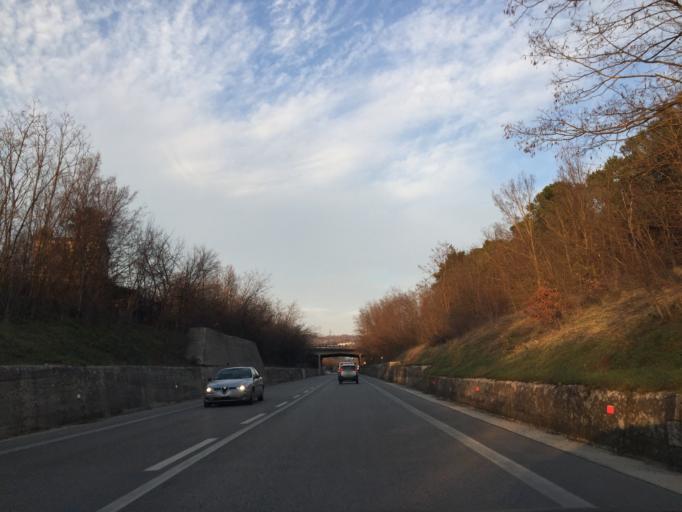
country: IT
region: Molise
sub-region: Provincia di Campobasso
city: Vinchiaturo
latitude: 41.4904
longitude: 14.6001
